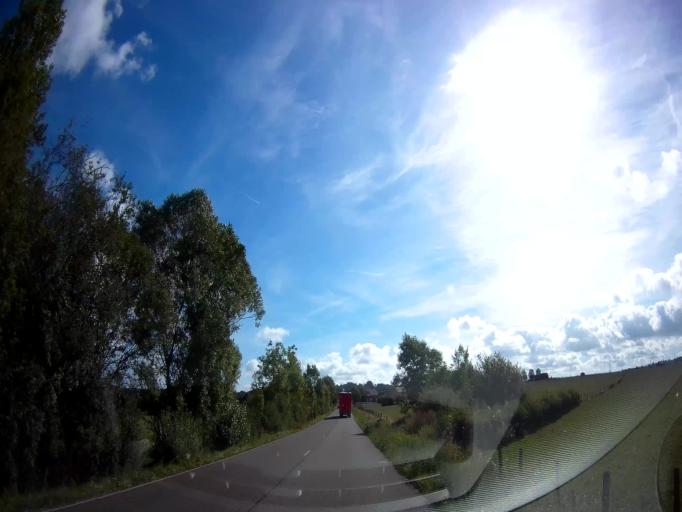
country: BE
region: Wallonia
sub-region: Province de Namur
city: Rochefort
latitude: 50.1672
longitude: 5.1999
